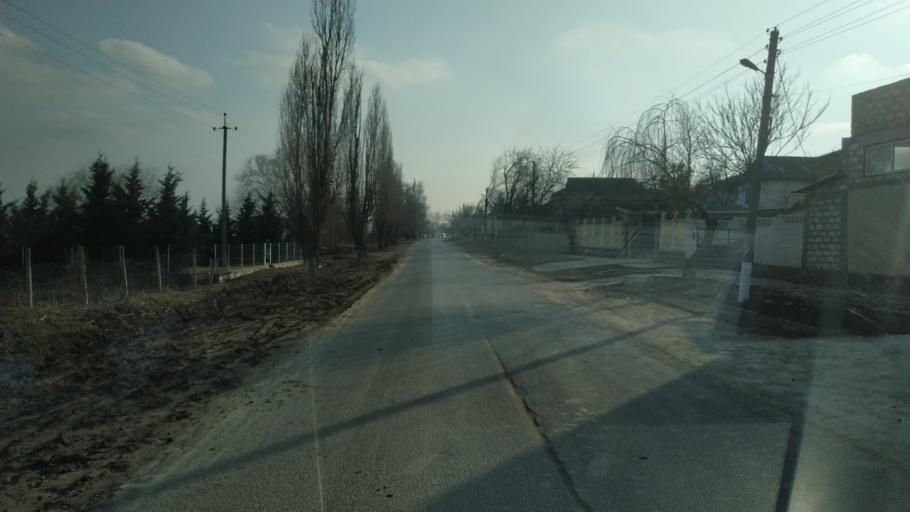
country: MD
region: Hincesti
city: Dancu
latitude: 46.7808
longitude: 28.3487
